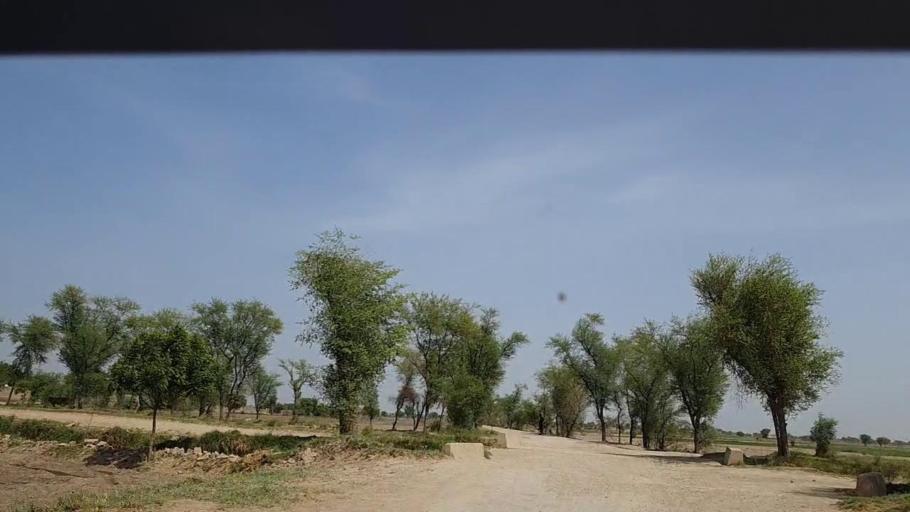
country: PK
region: Sindh
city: Phulji
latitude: 26.9552
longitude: 67.7112
